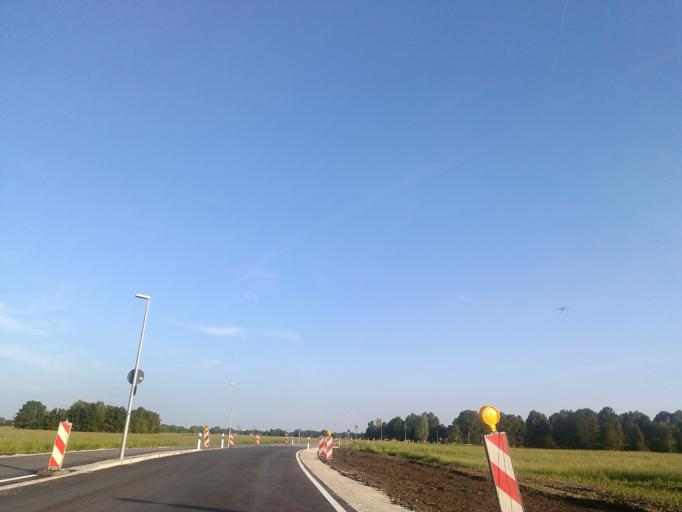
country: DE
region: Bavaria
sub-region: Upper Bavaria
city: Grobenzell
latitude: 48.1922
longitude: 11.4079
